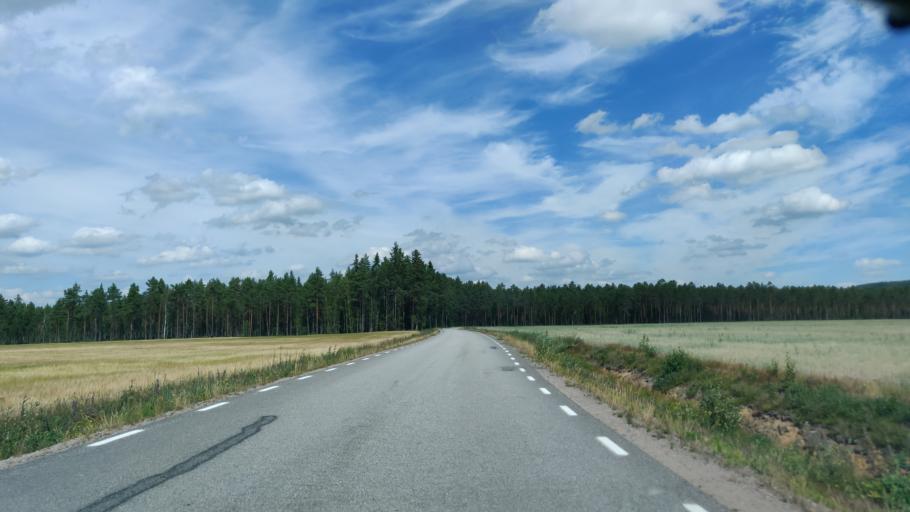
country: SE
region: Vaermland
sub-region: Hagfors Kommun
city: Ekshaerad
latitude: 60.0743
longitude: 13.4944
